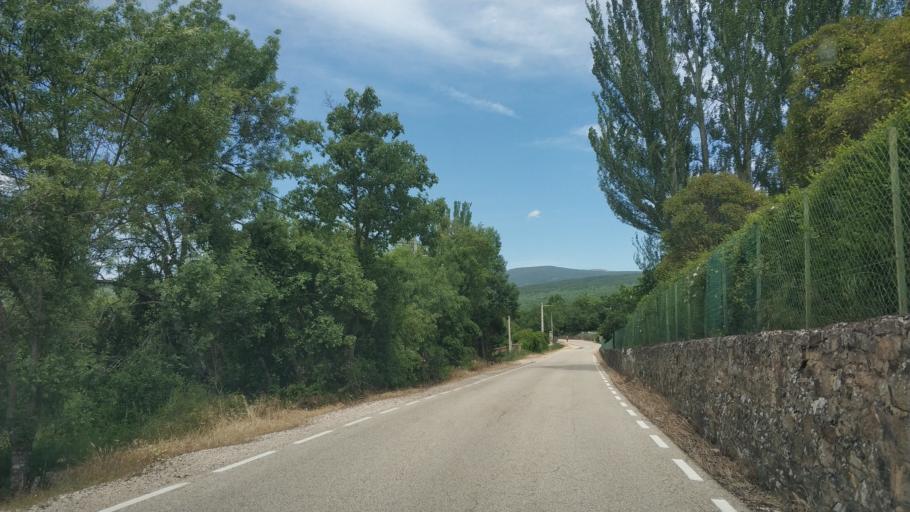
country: ES
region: Castille and Leon
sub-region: Provincia de Soria
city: Sotillo del Rincon
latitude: 41.8983
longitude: -2.6390
